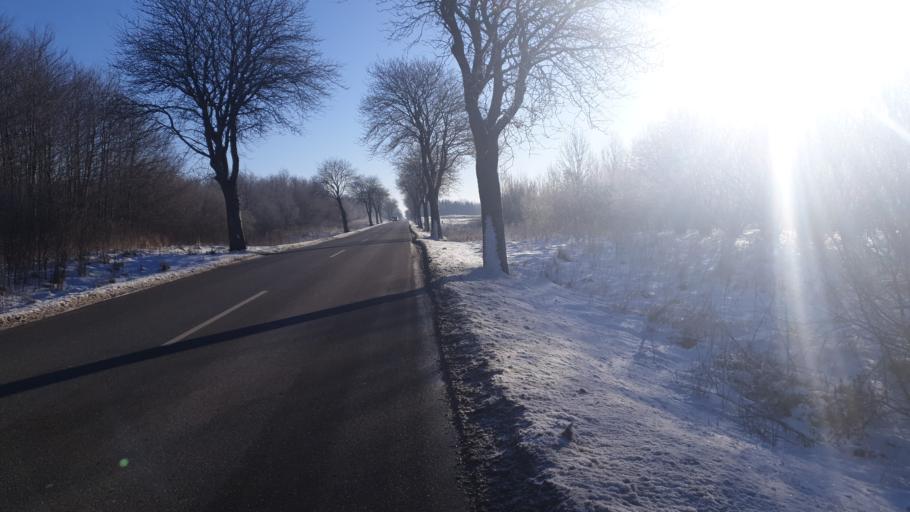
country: DK
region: Central Jutland
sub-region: Hedensted Kommune
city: Hedensted
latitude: 55.8024
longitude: 9.7132
